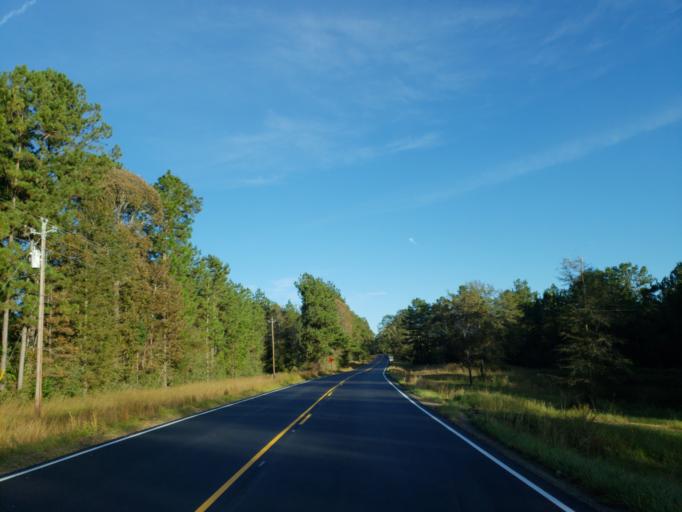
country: US
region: Mississippi
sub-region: Perry County
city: Richton
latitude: 31.3488
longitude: -88.7796
